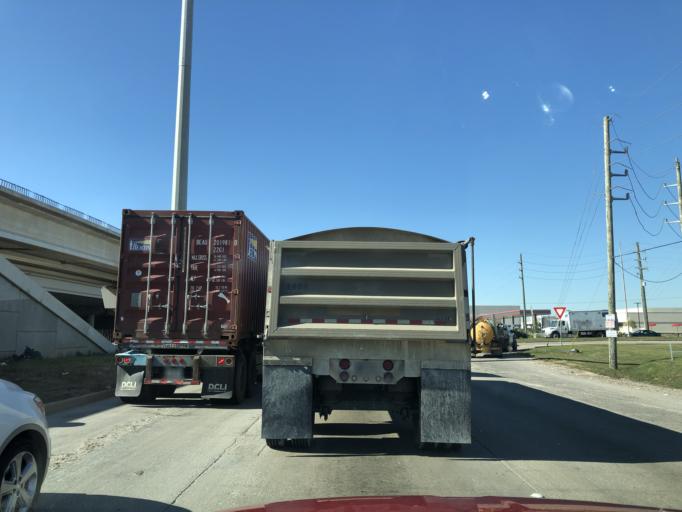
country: US
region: Texas
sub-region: Brazoria County
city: Brookside Village
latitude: 29.5985
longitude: -95.3676
